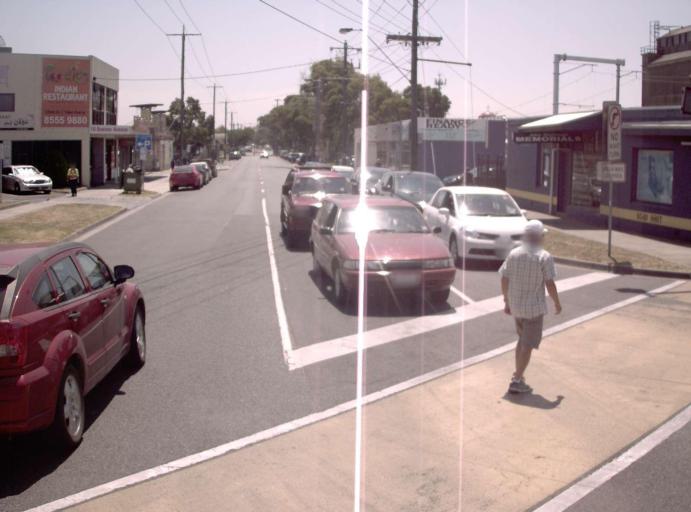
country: AU
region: Victoria
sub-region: Greater Dandenong
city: Springvale
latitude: -37.9493
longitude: 145.1527
